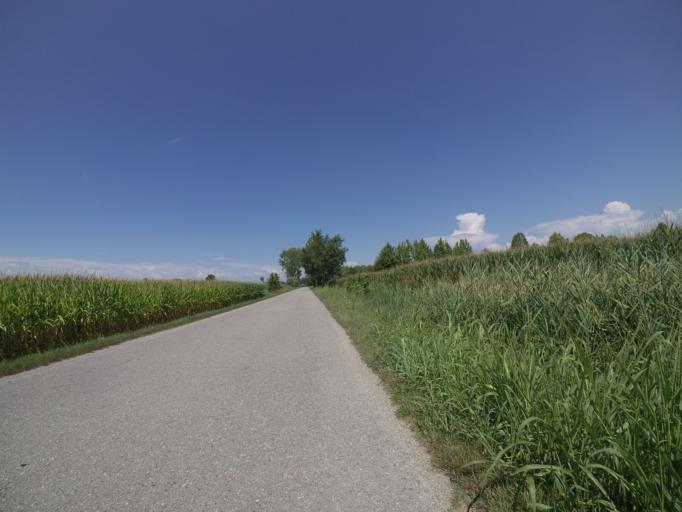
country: IT
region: Friuli Venezia Giulia
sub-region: Provincia di Udine
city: Talmassons
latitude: 45.9026
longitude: 13.1171
